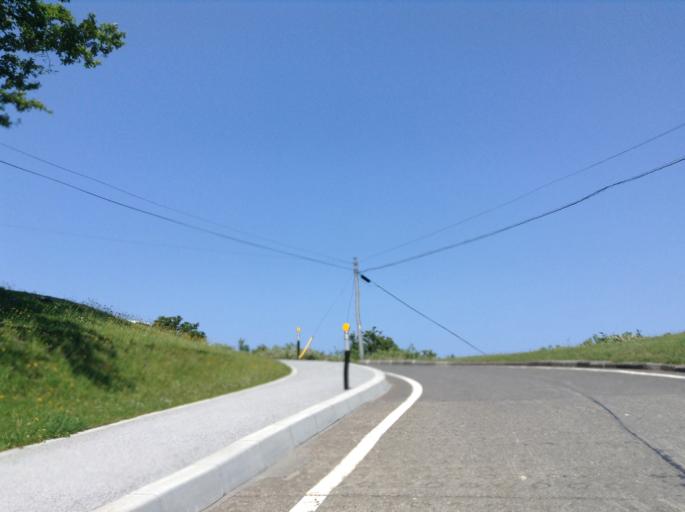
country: JP
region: Hokkaido
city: Wakkanai
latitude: 45.4200
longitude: 141.6689
